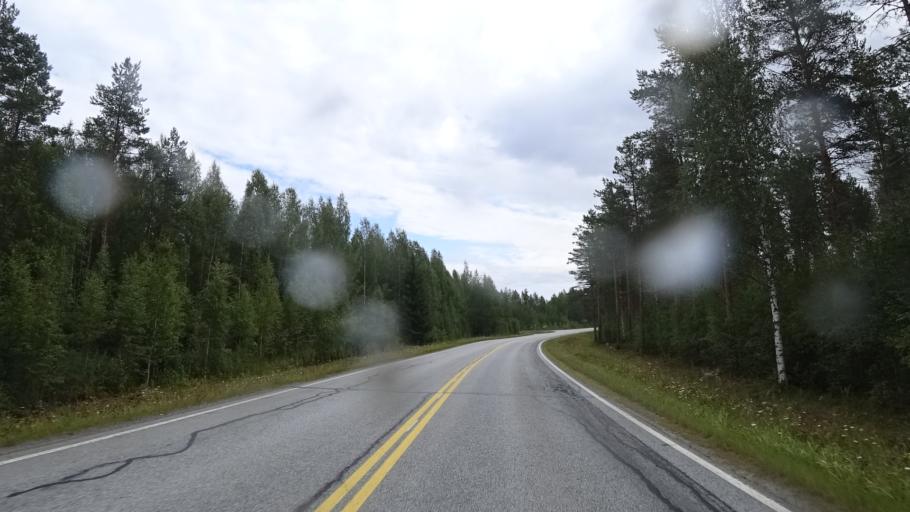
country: FI
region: North Karelia
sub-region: Keski-Karjala
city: Raeaekkylae
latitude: 62.1101
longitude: 29.7152
